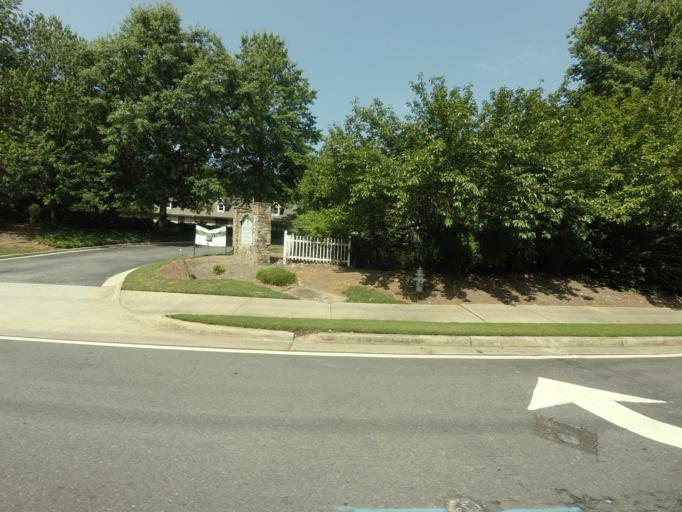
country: US
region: Georgia
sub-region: Fulton County
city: Alpharetta
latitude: 34.0029
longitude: -84.2765
